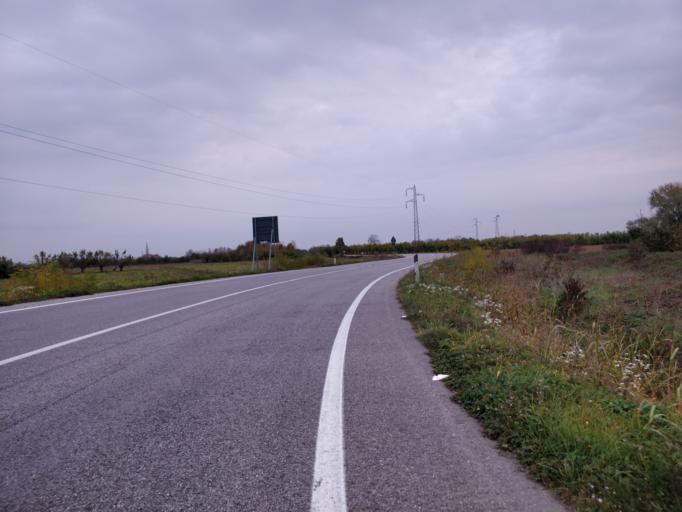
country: IT
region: Friuli Venezia Giulia
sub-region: Provincia di Udine
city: Talmassons
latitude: 45.9353
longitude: 13.1363
